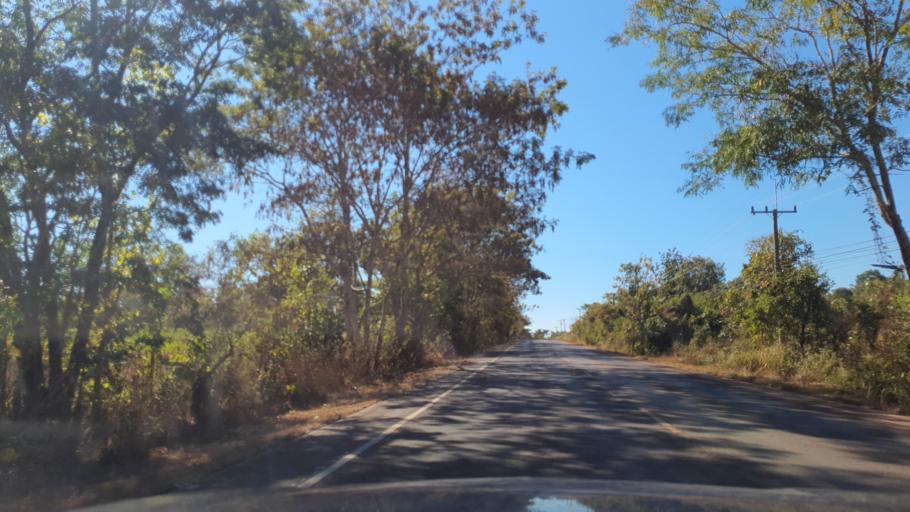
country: TH
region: Nakhon Phanom
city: Si Songkhram
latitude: 17.7389
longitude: 104.2861
